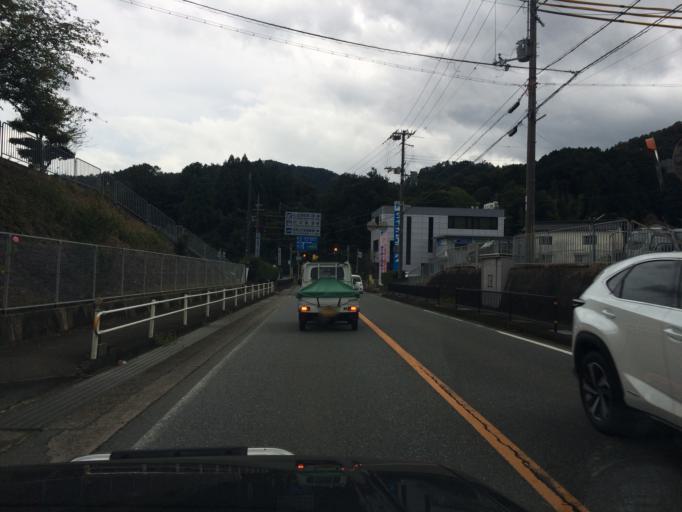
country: JP
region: Hyogo
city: Toyooka
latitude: 35.4048
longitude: 134.7773
